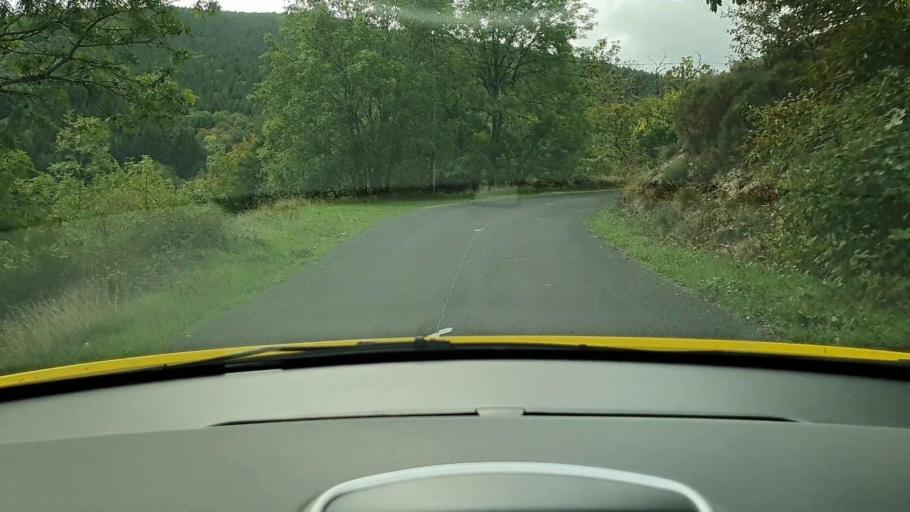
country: FR
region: Languedoc-Roussillon
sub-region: Departement de la Lozere
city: Meyrueis
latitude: 44.0633
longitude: 3.4490
